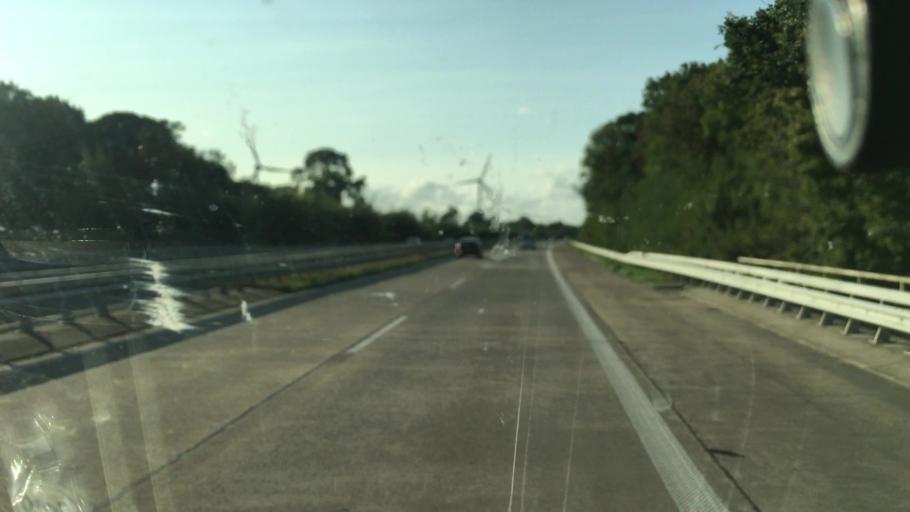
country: DE
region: Lower Saxony
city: Bockhorn
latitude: 53.4344
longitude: 8.0440
